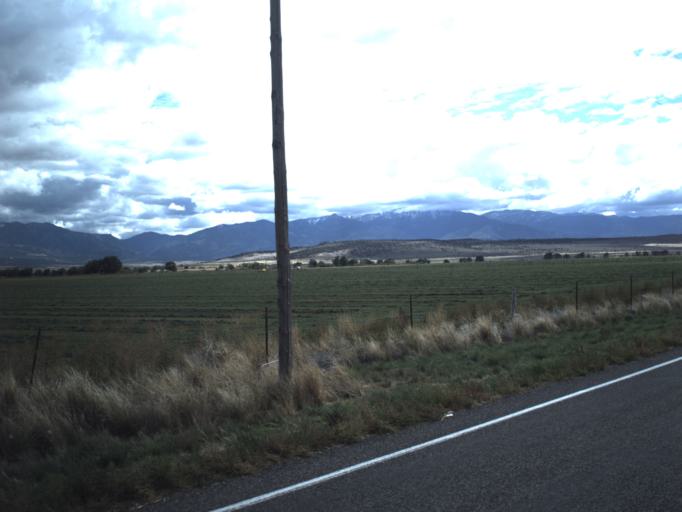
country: US
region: Utah
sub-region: Millard County
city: Fillmore
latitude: 39.0554
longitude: -112.4098
